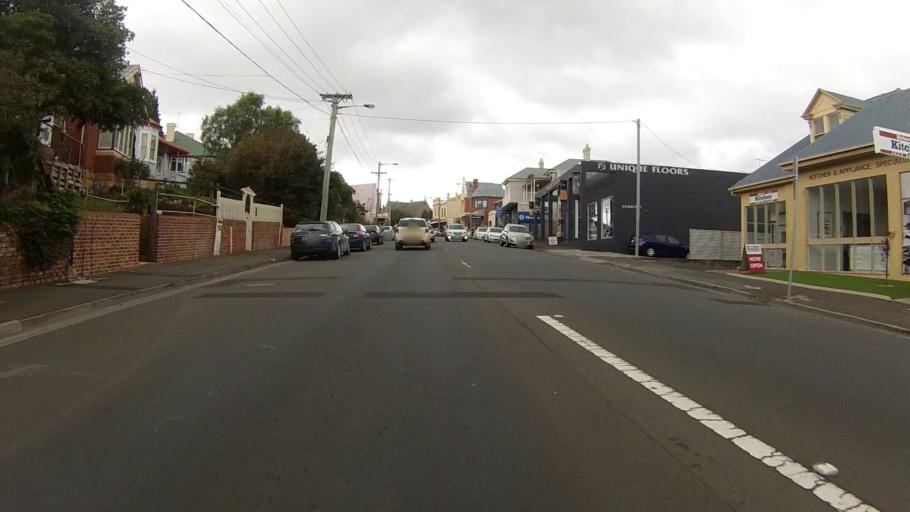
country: AU
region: Tasmania
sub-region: Hobart
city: New Town
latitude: -42.8575
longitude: 147.3042
